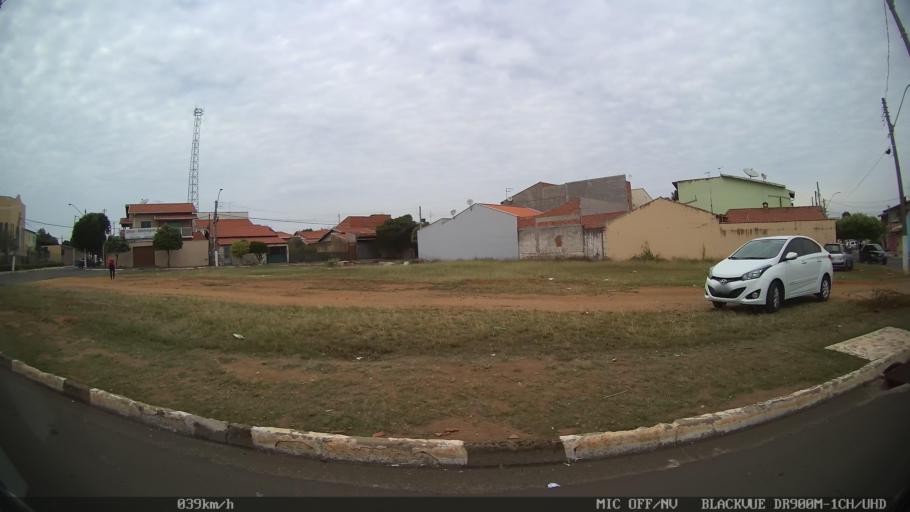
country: BR
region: Sao Paulo
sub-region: Paulinia
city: Paulinia
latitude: -22.7232
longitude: -47.1762
